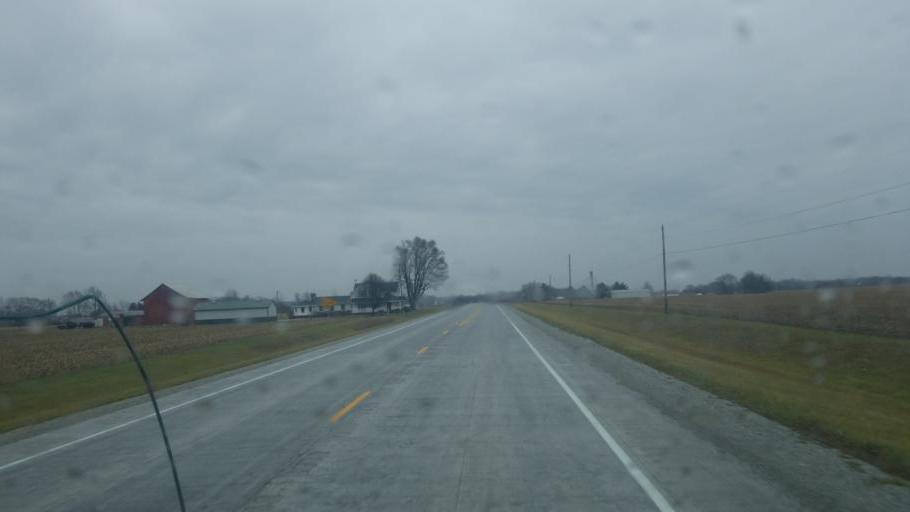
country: US
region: Indiana
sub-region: Shelby County
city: Geneva
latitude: 39.3798
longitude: -85.7607
